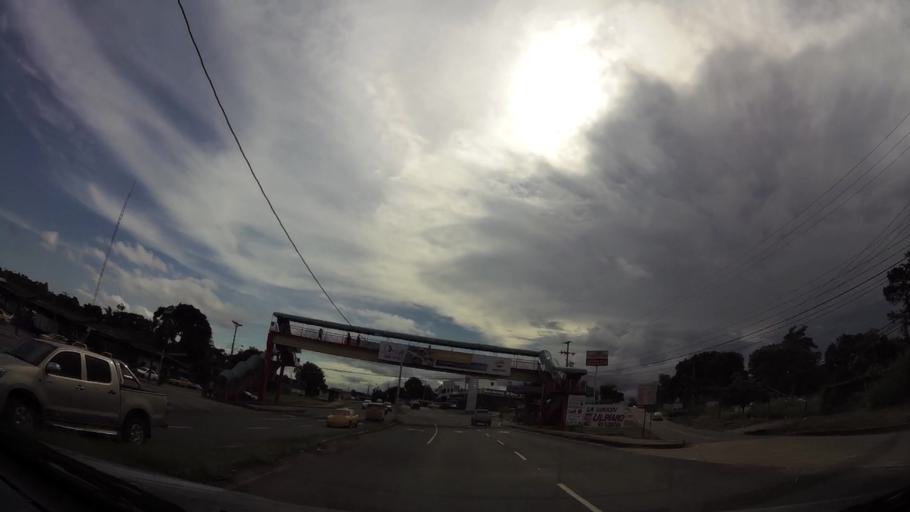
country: PA
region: Panama
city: El Coco
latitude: 8.8708
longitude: -79.8013
